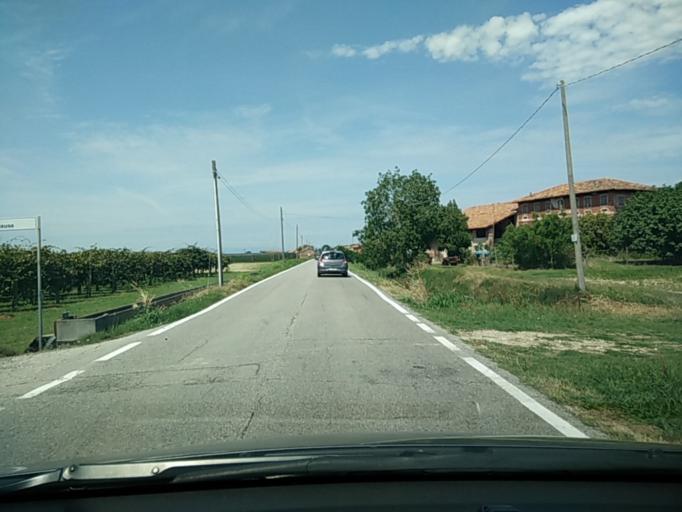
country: IT
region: Veneto
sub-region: Provincia di Venezia
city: Passarella
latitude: 45.5675
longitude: 12.6280
